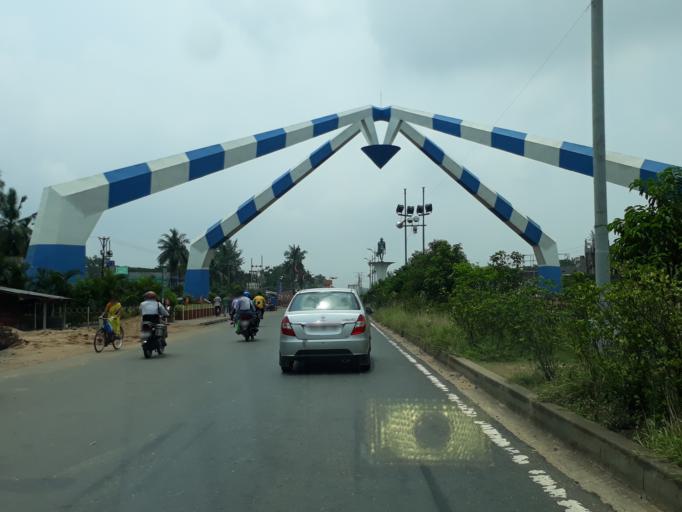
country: IN
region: West Bengal
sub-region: Purba Medinipur
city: Monoharpur
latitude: 22.0911
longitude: 88.0396
